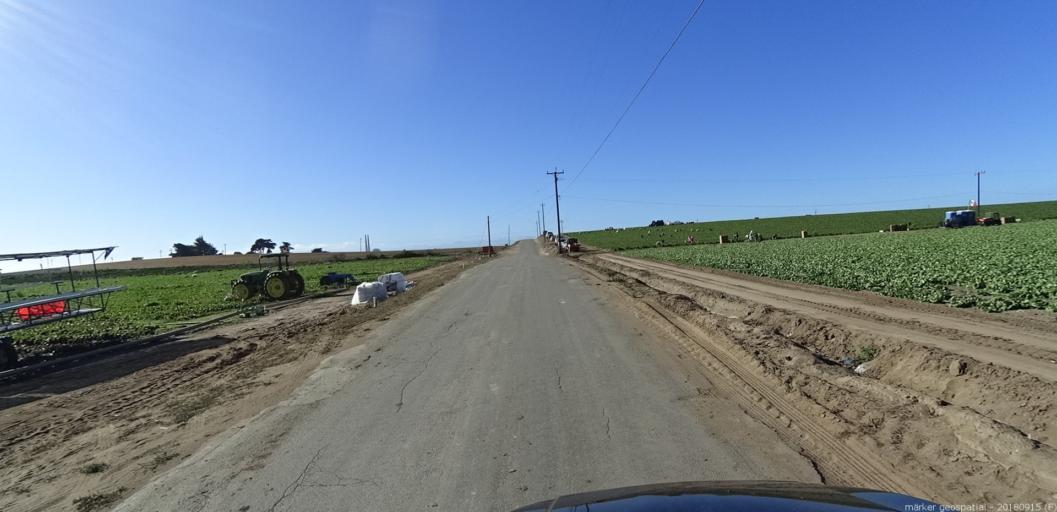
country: US
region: California
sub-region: Monterey County
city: Elkhorn
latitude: 36.8334
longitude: -121.7936
